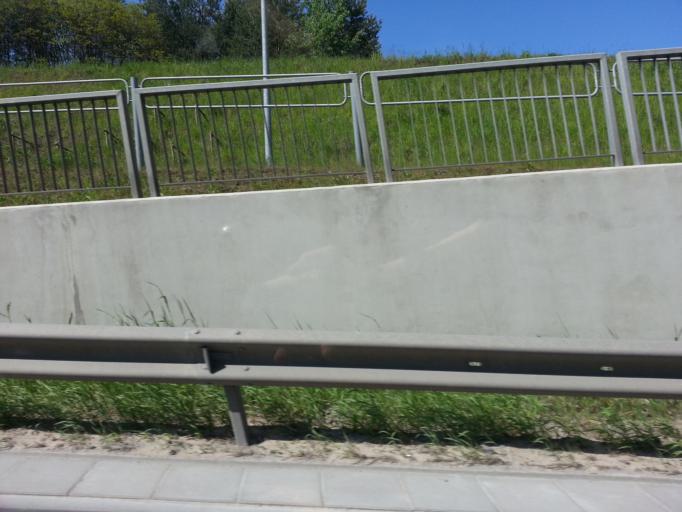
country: LT
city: Baltoji Voke
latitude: 54.6362
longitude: 25.1516
